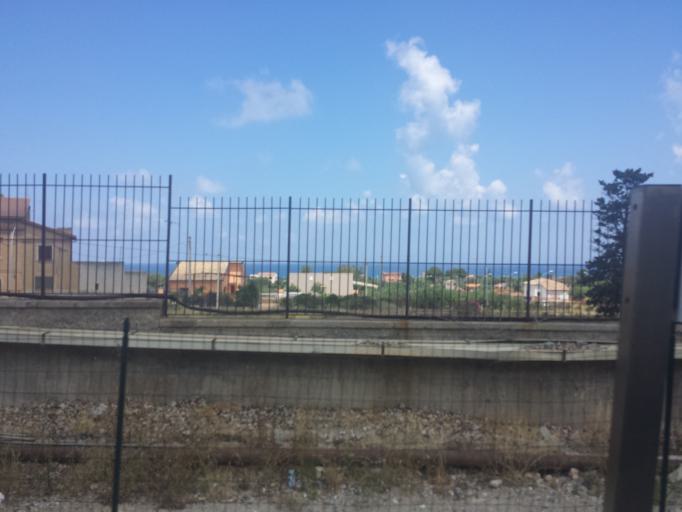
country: IT
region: Sicily
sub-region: Palermo
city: Capaci
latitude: 38.1712
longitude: 13.2312
